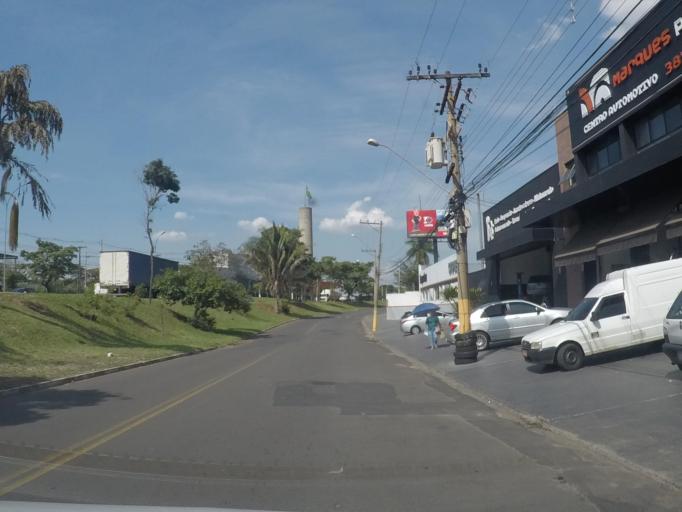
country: BR
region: Sao Paulo
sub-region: Sumare
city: Sumare
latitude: -22.8083
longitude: -47.2544
